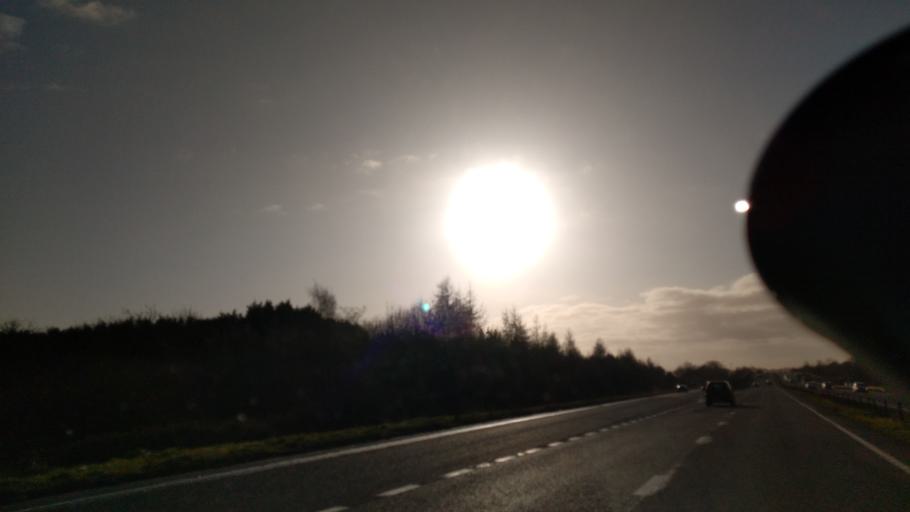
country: GB
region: England
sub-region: Borough of Swindon
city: Wanborough
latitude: 51.5458
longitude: -1.7215
